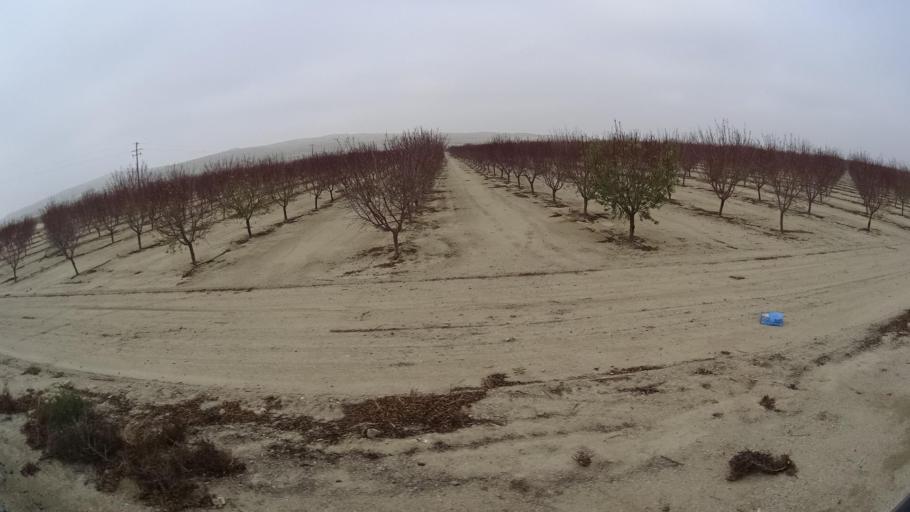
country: US
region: California
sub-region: Kern County
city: Maricopa
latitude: 35.1231
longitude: -119.3580
